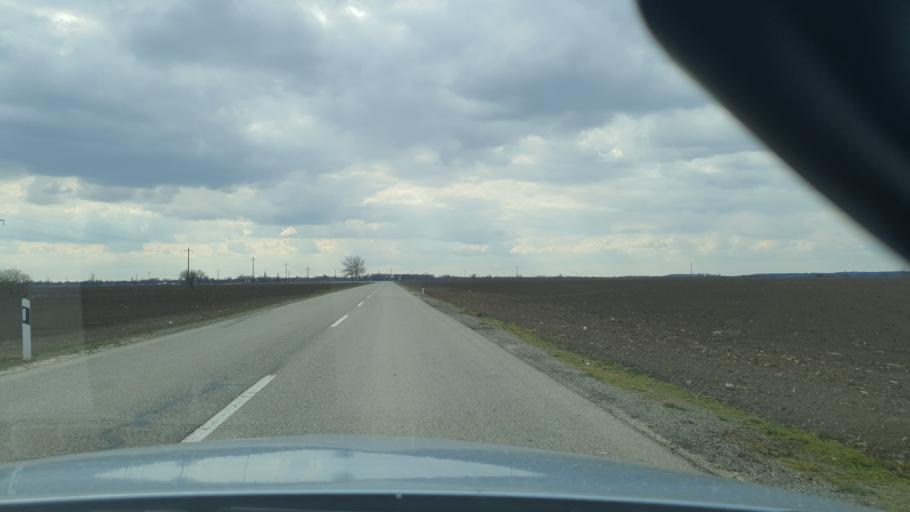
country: RS
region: Autonomna Pokrajina Vojvodina
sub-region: Juznobacki Okrug
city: Bac
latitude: 45.4303
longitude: 19.3090
